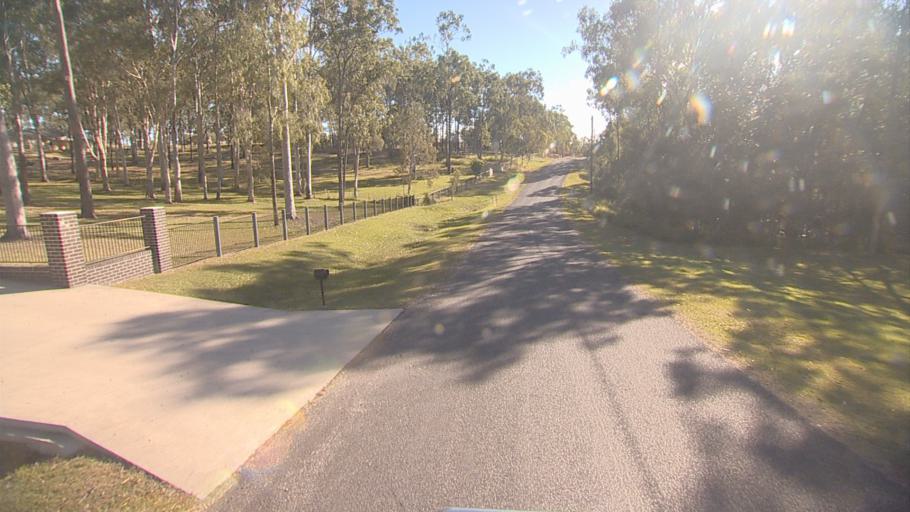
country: AU
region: Queensland
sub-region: Ipswich
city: Springfield Lakes
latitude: -27.6960
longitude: 152.9276
